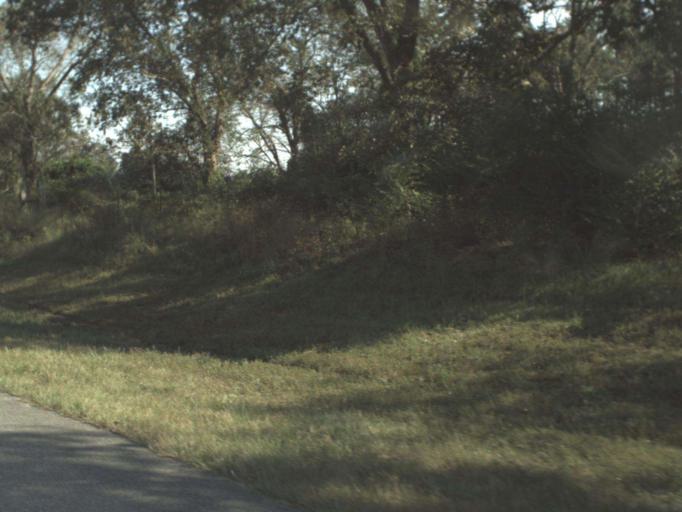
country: US
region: Florida
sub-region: Jackson County
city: Graceville
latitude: 30.9285
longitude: -85.6491
